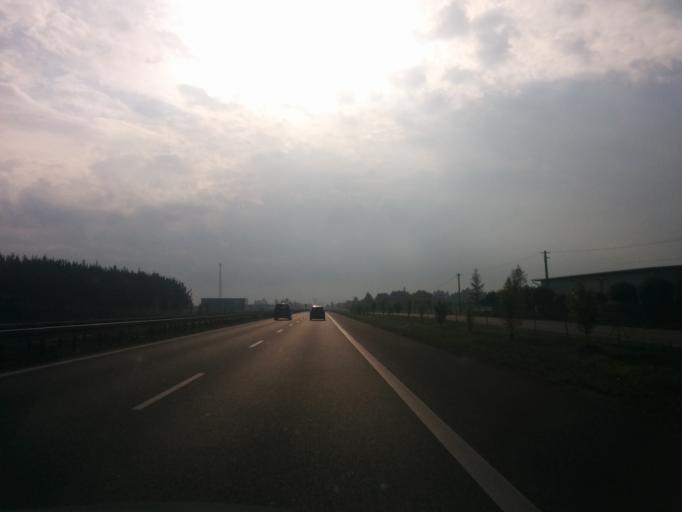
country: PL
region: Masovian Voivodeship
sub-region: Powiat radomski
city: Jedlinsk
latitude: 51.5273
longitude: 21.0904
